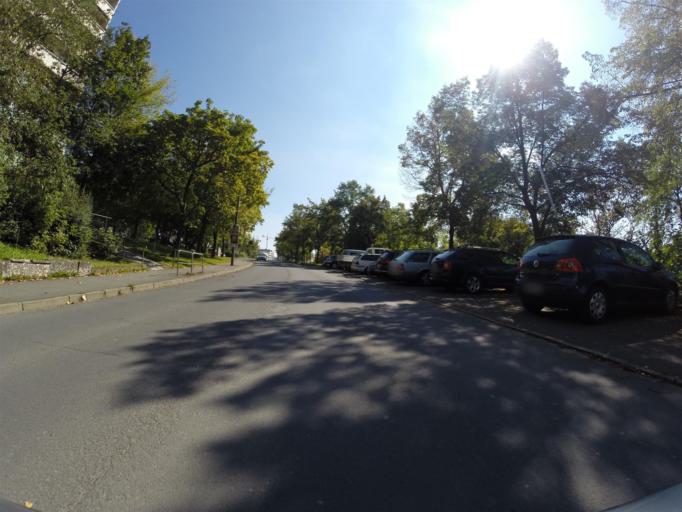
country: DE
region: Thuringia
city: Sulza
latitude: 50.8888
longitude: 11.6142
